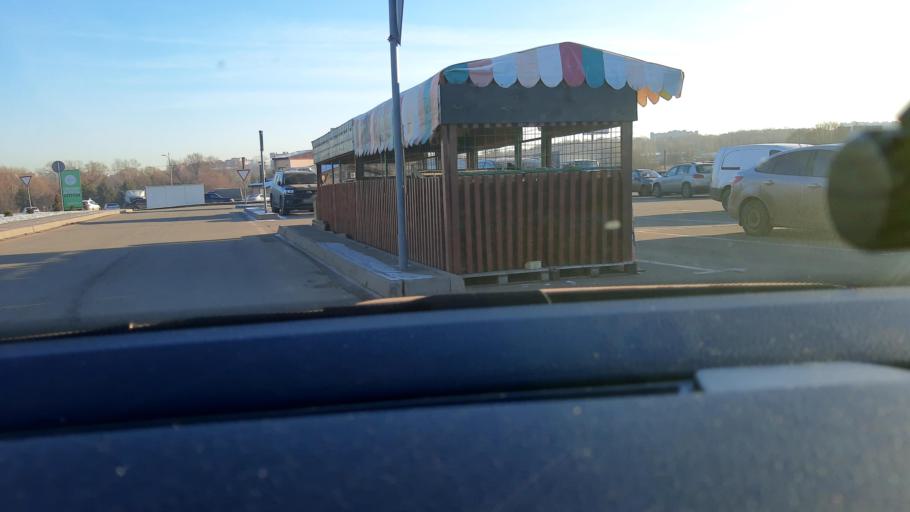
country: RU
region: Moscow
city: Vatutino
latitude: 55.8972
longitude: 37.6835
